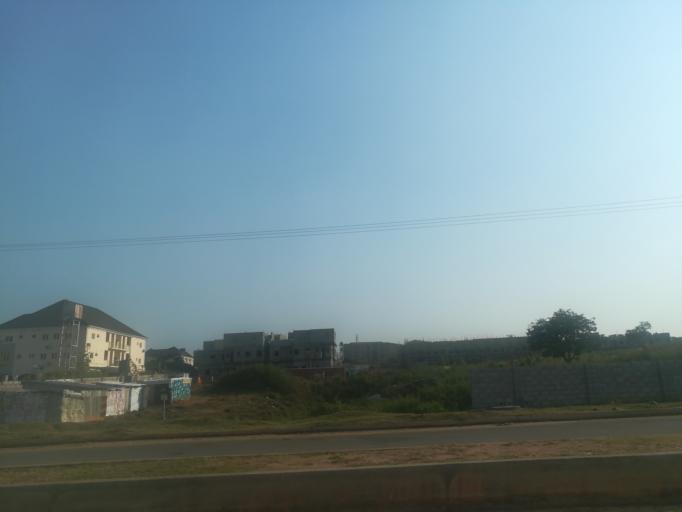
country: NG
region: Abuja Federal Capital Territory
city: Abuja
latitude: 9.0452
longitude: 7.4363
